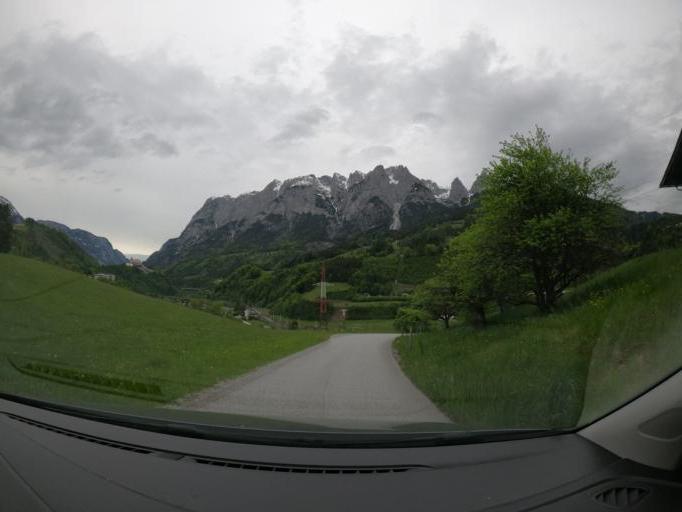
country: AT
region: Salzburg
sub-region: Politischer Bezirk Sankt Johann im Pongau
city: Werfen
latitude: 47.4675
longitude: 13.1939
